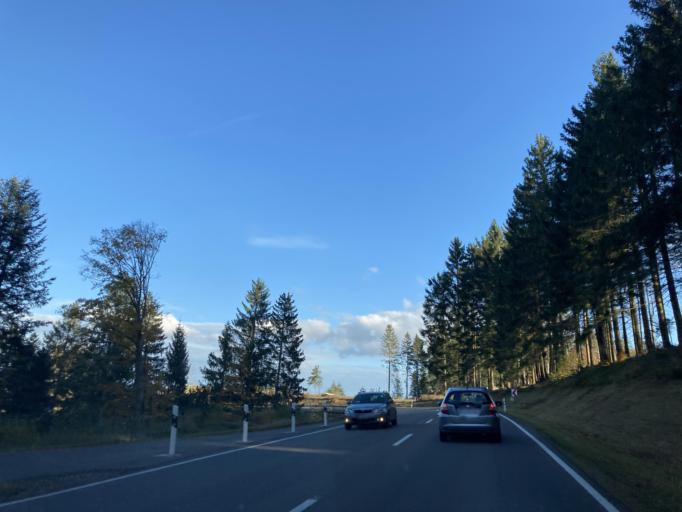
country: DE
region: Baden-Wuerttemberg
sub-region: Freiburg Region
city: Gutenbach
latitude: 47.9903
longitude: 8.1618
